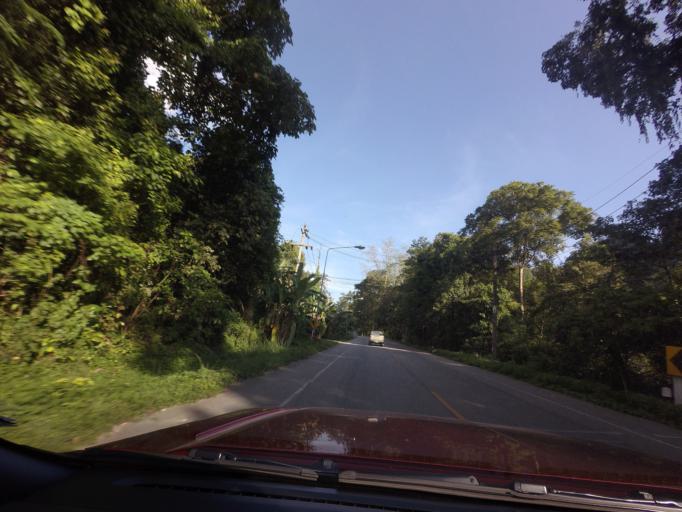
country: TH
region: Yala
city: Than To
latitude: 6.1798
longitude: 101.1743
